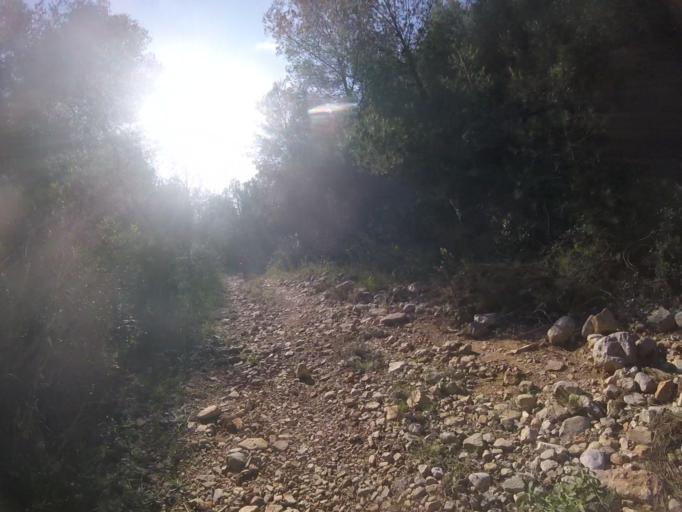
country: ES
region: Valencia
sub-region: Provincia de Castello
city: Santa Magdalena de Pulpis
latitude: 40.3111
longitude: 0.3335
